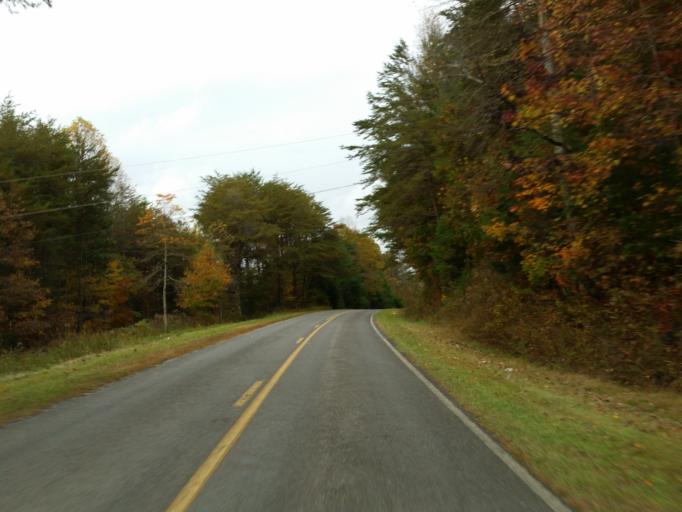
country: US
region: Georgia
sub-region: Fannin County
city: Blue Ridge
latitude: 34.6748
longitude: -84.2757
